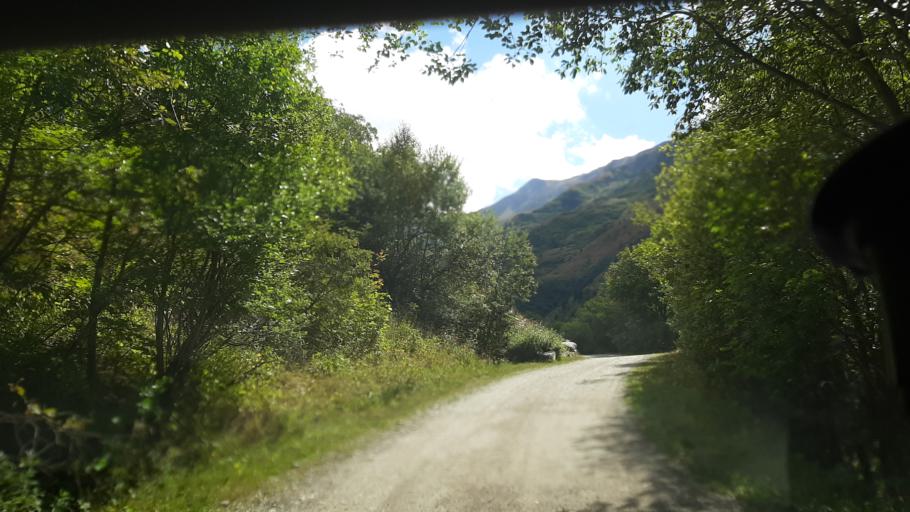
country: FR
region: Rhone-Alpes
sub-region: Departement de la Savoie
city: Saint-Michel-de-Maurienne
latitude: 45.1671
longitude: 6.4942
